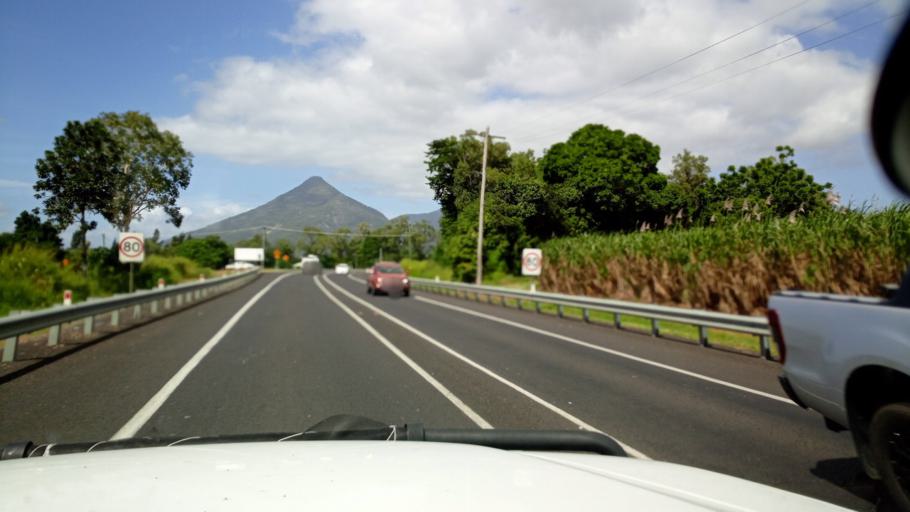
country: AU
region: Queensland
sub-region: Cairns
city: Woree
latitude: -17.0739
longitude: 145.7749
